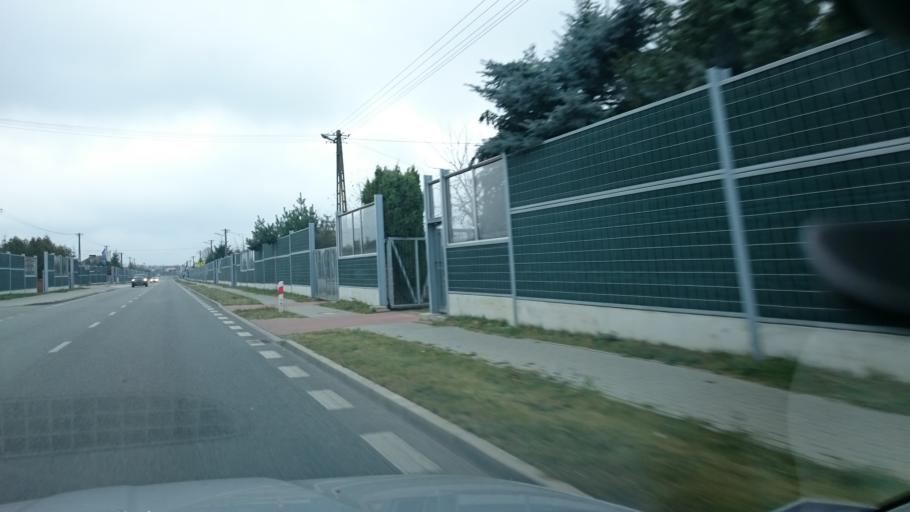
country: PL
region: Swietokrzyskie
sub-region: Powiat konecki
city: Konskie
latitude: 51.1630
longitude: 20.3727
